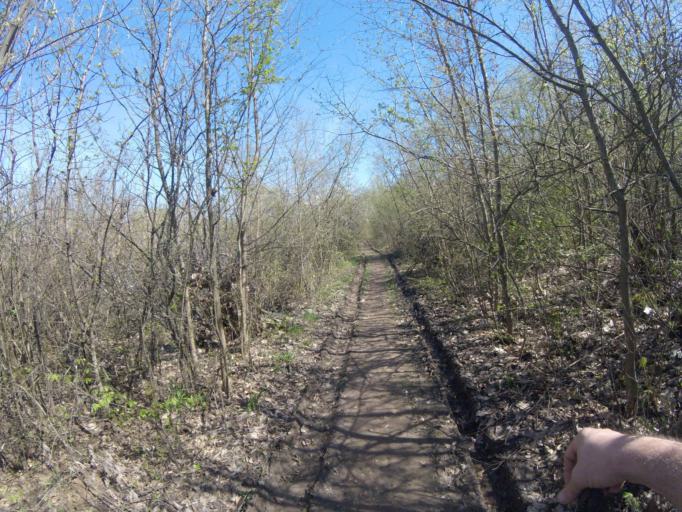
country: HU
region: Borsod-Abauj-Zemplen
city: Szendro
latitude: 48.4067
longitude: 20.7579
